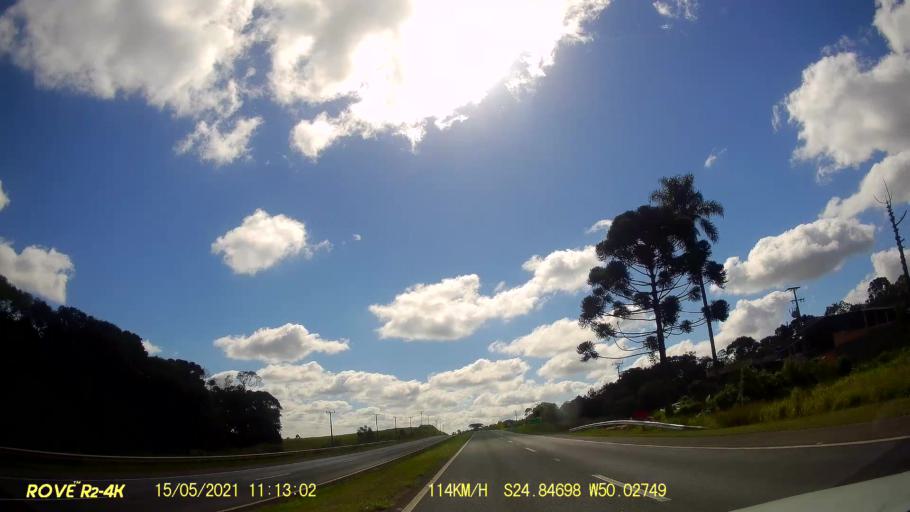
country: BR
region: Parana
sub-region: Castro
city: Castro
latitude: -24.8473
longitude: -50.0276
